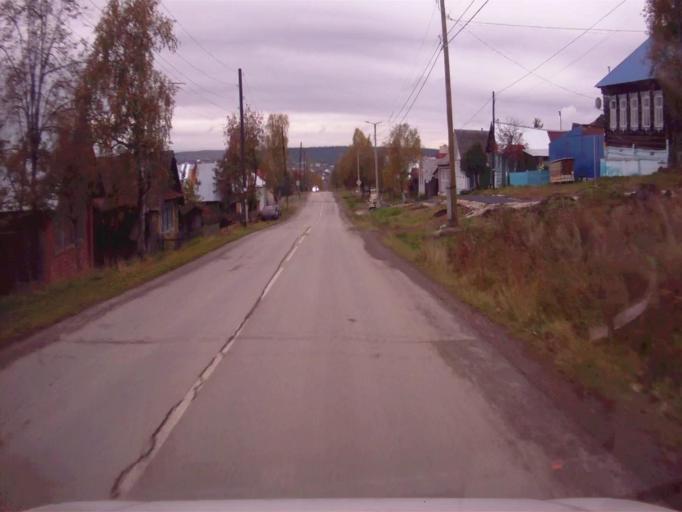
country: RU
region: Chelyabinsk
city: Nyazepetrovsk
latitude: 56.0590
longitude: 59.6101
